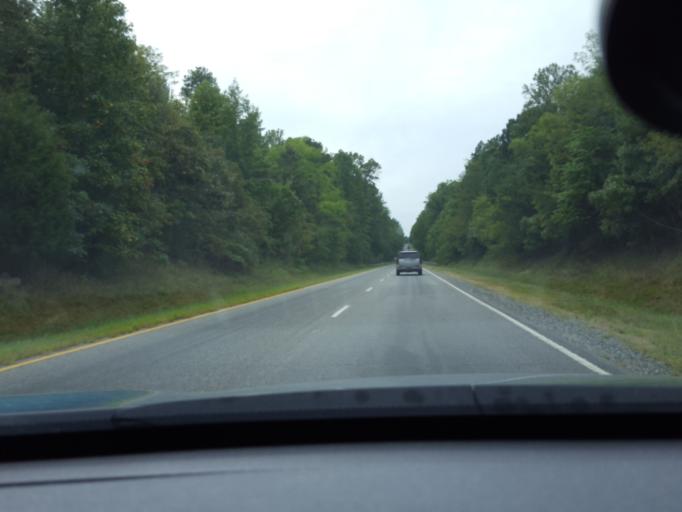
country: US
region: Virginia
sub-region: Caroline County
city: Bowling Green
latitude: 38.0988
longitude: -77.2782
